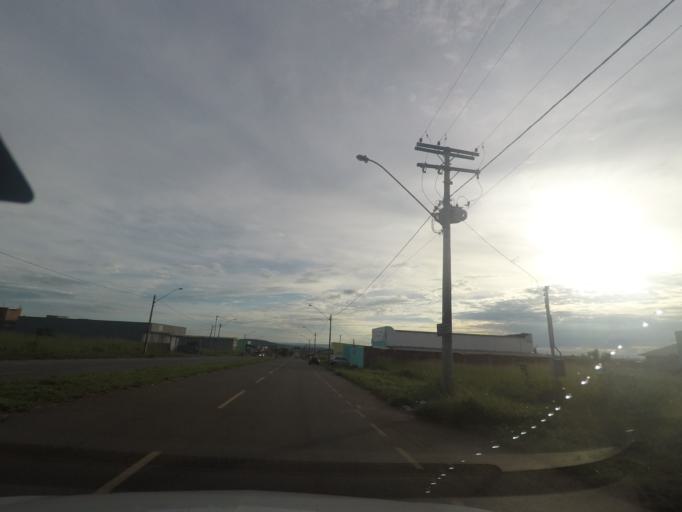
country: BR
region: Goias
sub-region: Trindade
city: Trindade
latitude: -16.7277
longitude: -49.4080
